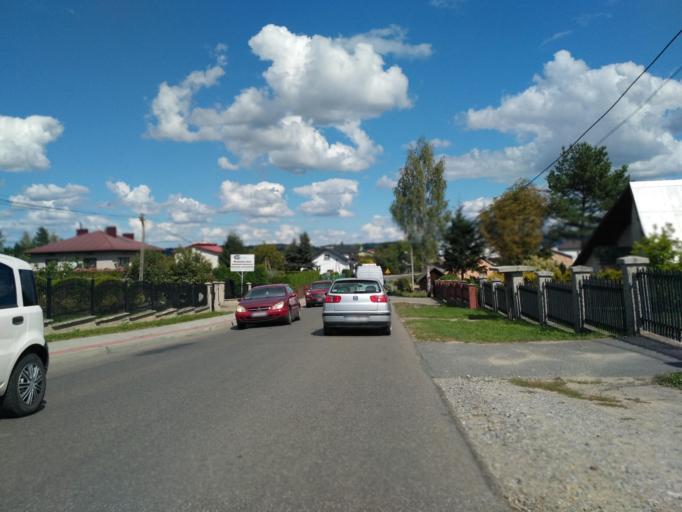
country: PL
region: Subcarpathian Voivodeship
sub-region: Powiat jasielski
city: Trzcinica
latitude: 49.7501
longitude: 21.4393
